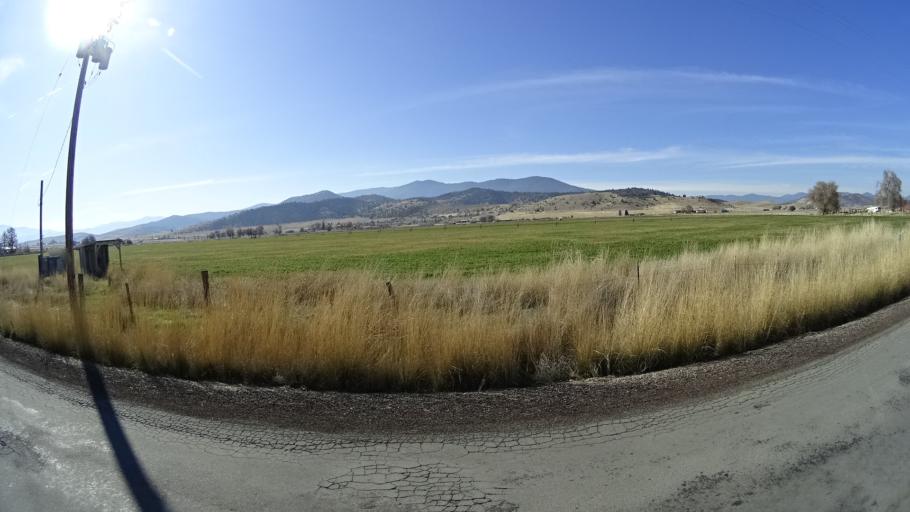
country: US
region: California
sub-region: Siskiyou County
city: Montague
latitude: 41.6384
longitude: -122.5216
